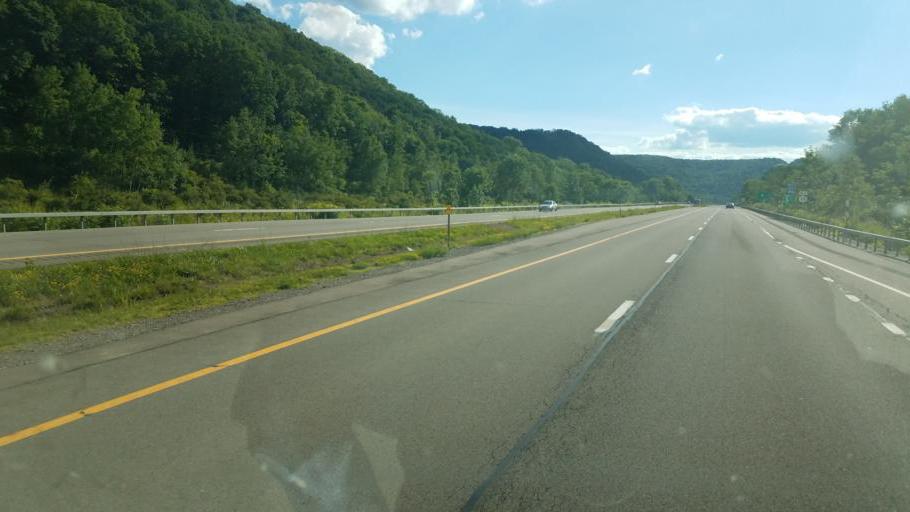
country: US
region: New York
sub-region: Cattaraugus County
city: Salamanca
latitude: 42.1065
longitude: -78.7855
